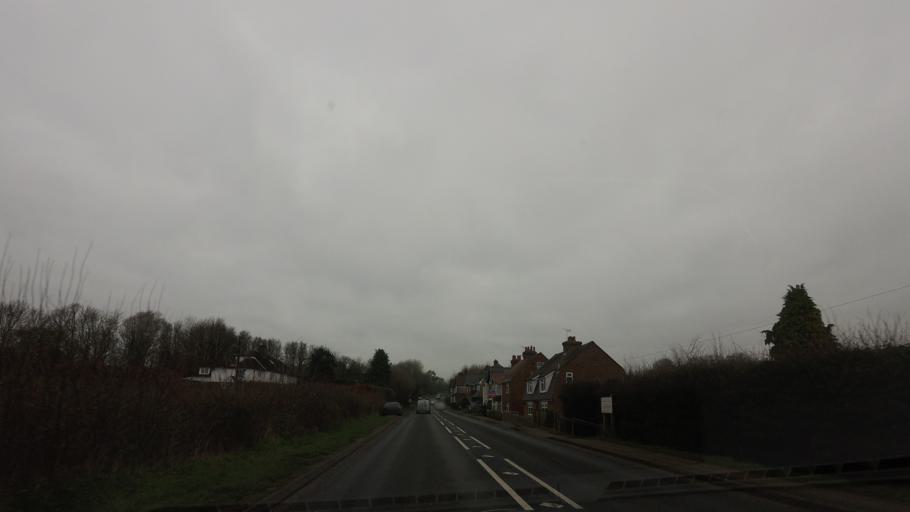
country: GB
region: England
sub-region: Kent
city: Cranbrook
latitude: 51.0819
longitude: 0.5091
